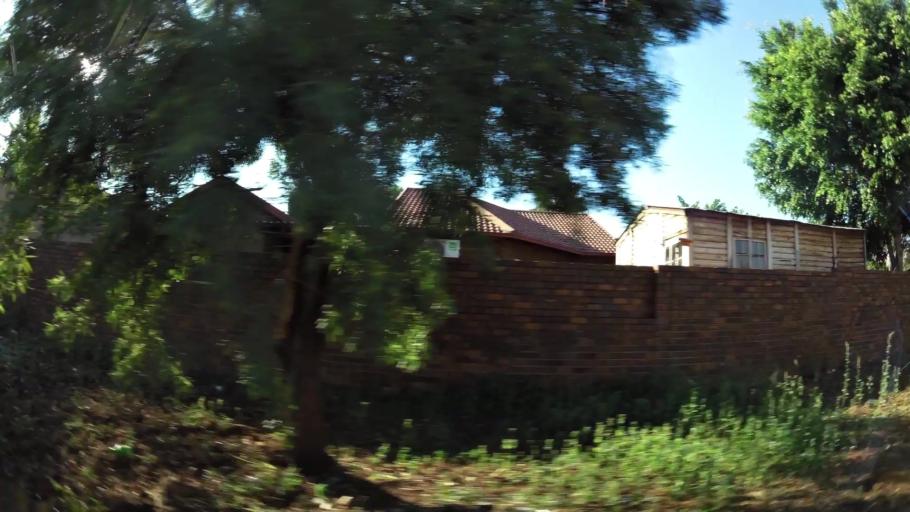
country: ZA
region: Gauteng
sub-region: City of Tshwane Metropolitan Municipality
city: Pretoria
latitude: -25.6719
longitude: 28.2217
